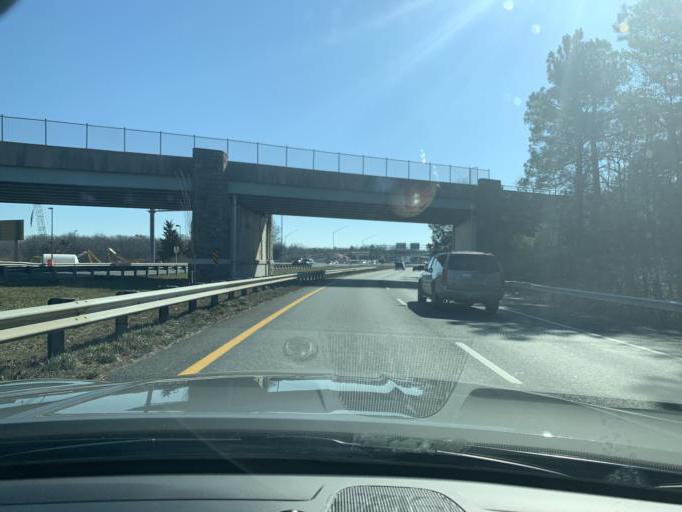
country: US
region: Maryland
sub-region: Prince George's County
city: Brandywine
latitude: 38.6964
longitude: -76.8727
